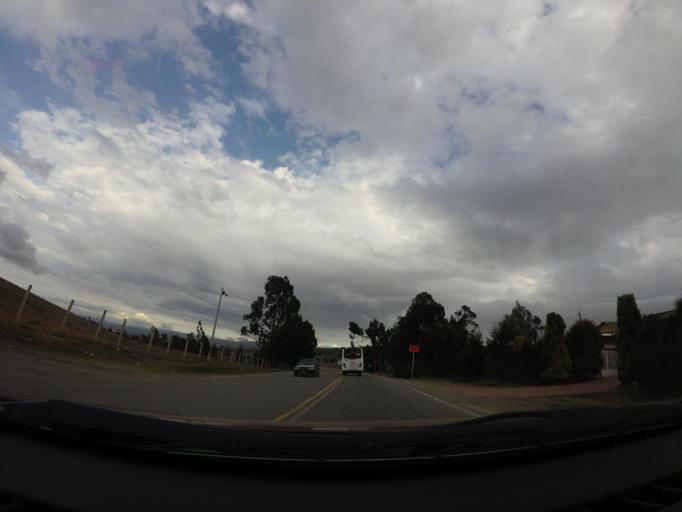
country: CO
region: Boyaca
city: Tunja
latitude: 5.5441
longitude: -73.3907
